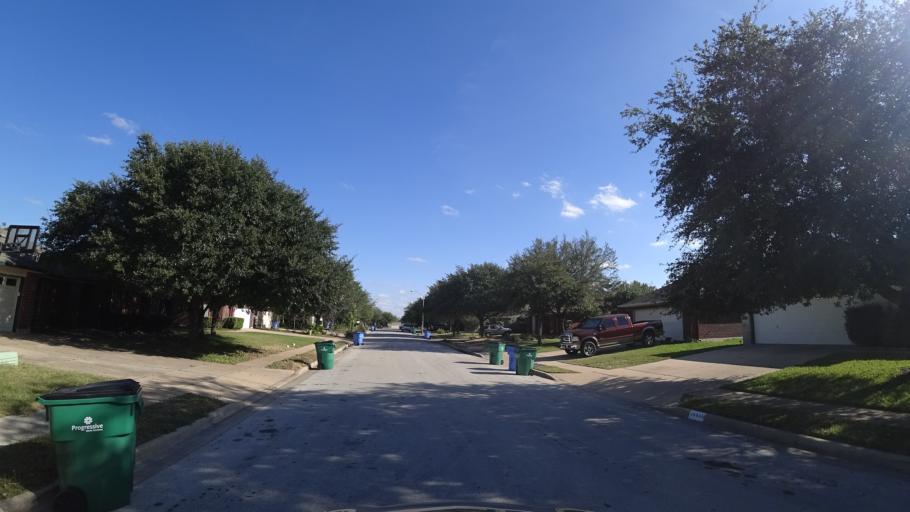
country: US
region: Texas
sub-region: Travis County
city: Wells Branch
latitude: 30.4653
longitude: -97.6861
